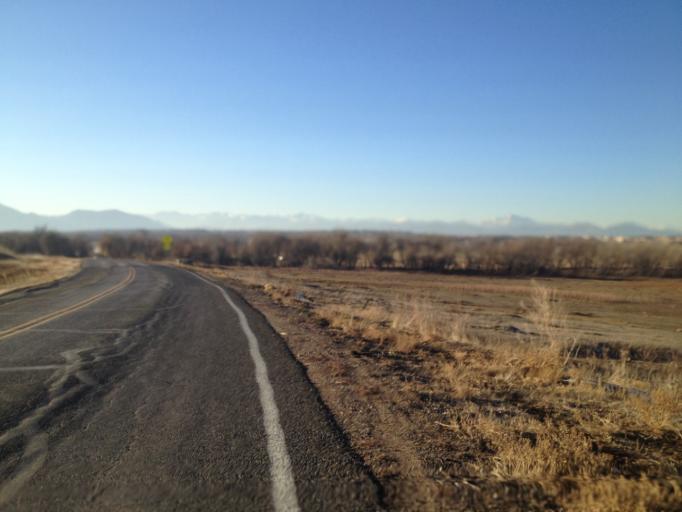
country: US
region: Colorado
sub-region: Boulder County
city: Louisville
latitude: 39.9761
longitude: -105.1103
